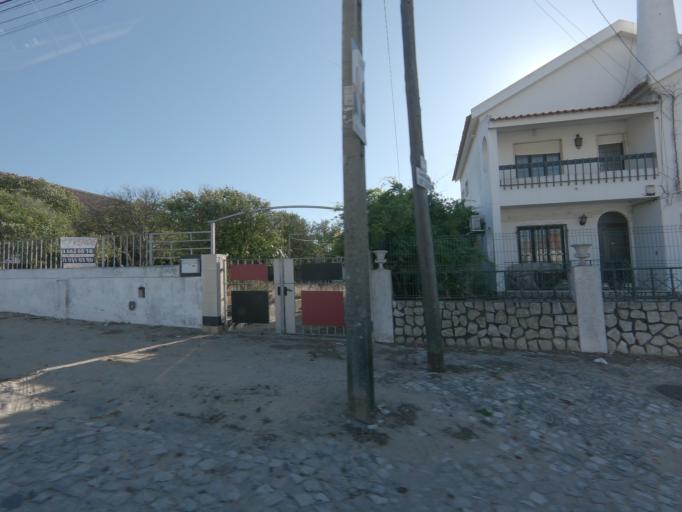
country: PT
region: Setubal
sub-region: Palmela
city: Palmela
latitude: 38.5763
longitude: -8.9072
